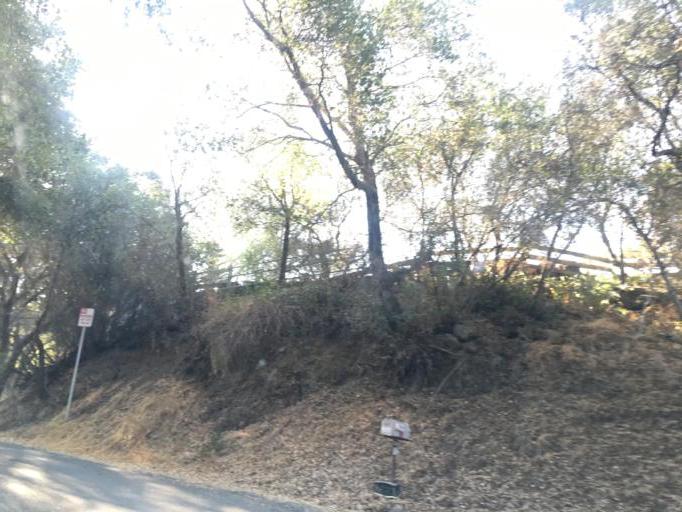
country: US
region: California
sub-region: Los Angeles County
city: Malibu Beach
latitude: 34.0785
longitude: -118.6882
